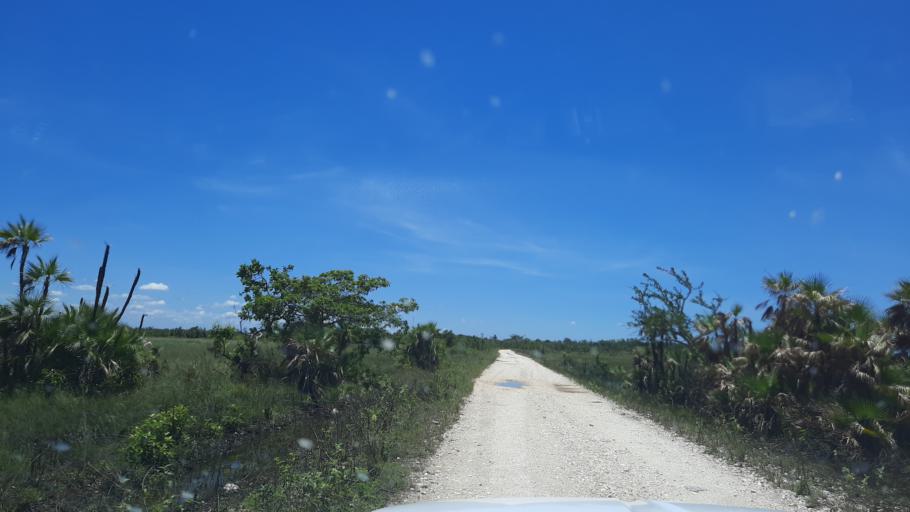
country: BZ
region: Cayo
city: Belmopan
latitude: 17.3918
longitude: -88.4900
